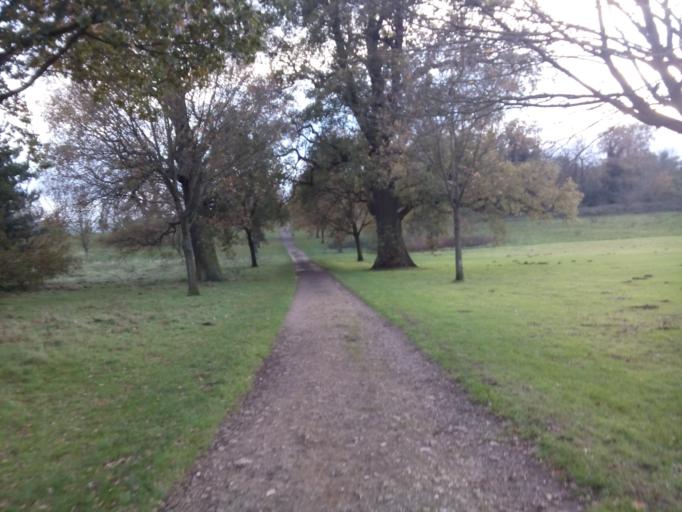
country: GB
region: England
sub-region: Suffolk
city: Bramford
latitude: 52.0529
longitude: 1.1160
